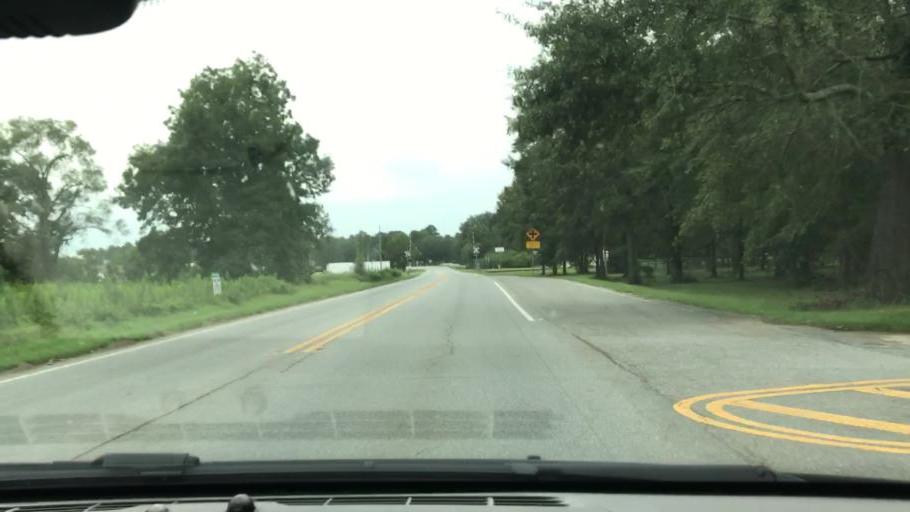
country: US
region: Georgia
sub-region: Early County
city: Blakely
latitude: 31.3731
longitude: -84.9578
